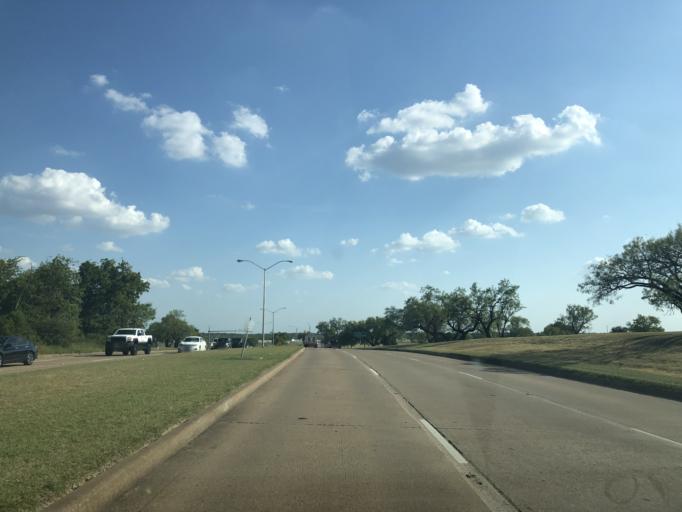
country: US
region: Texas
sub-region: Tarrant County
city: Sansom Park
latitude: 32.8319
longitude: -97.3853
